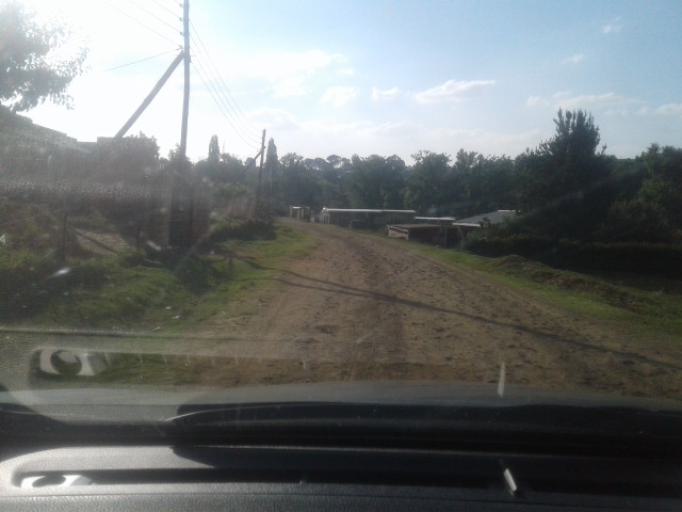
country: LS
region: Berea
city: Teyateyaneng
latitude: -29.1547
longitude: 27.7544
